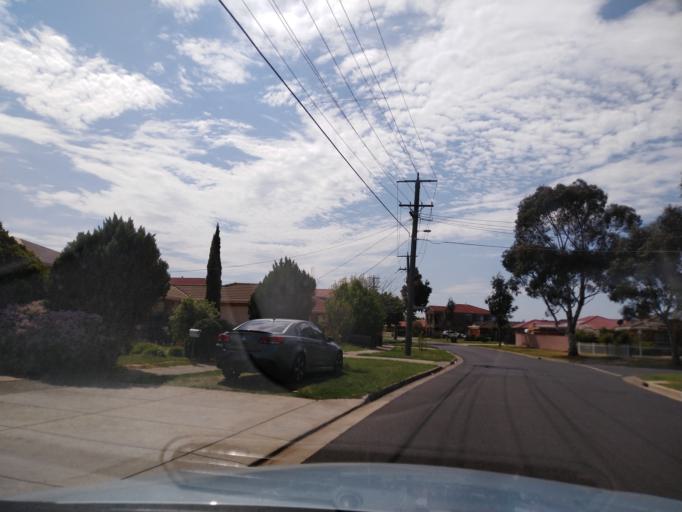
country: AU
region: Victoria
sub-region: Wyndham
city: Hoppers Crossing
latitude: -37.8629
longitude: 144.7163
